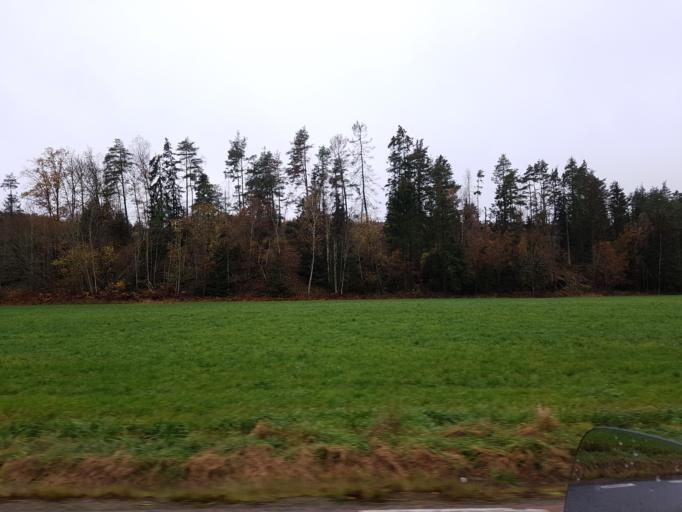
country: SE
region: Vaestra Goetaland
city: Svanesund
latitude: 58.1985
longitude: 11.8257
